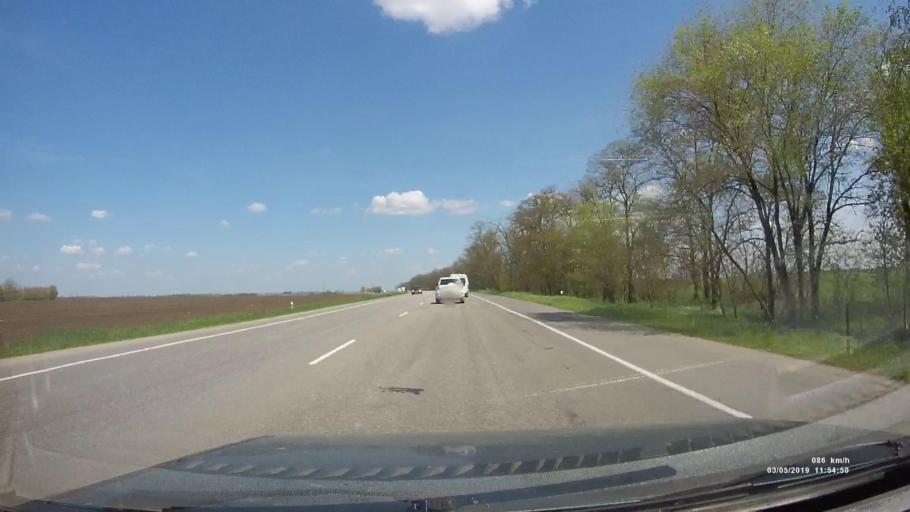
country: RU
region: Rostov
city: Bagayevskaya
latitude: 47.1738
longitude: 40.2853
